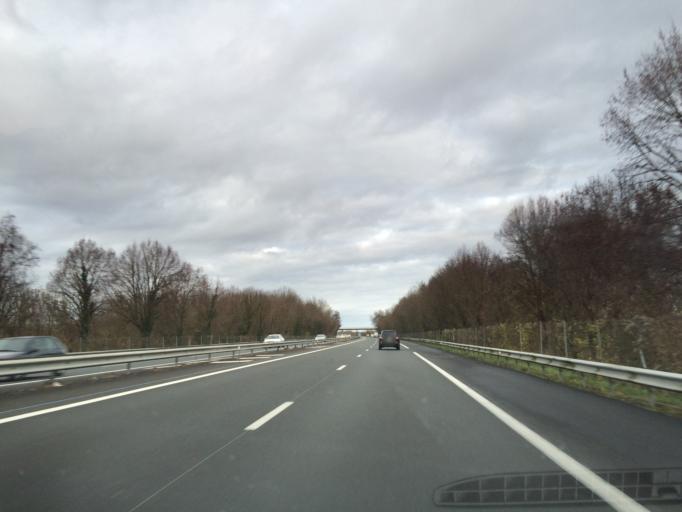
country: FR
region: Poitou-Charentes
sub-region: Departement des Deux-Sevres
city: Beauvoir-sur-Niort
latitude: 46.2113
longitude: -0.4601
